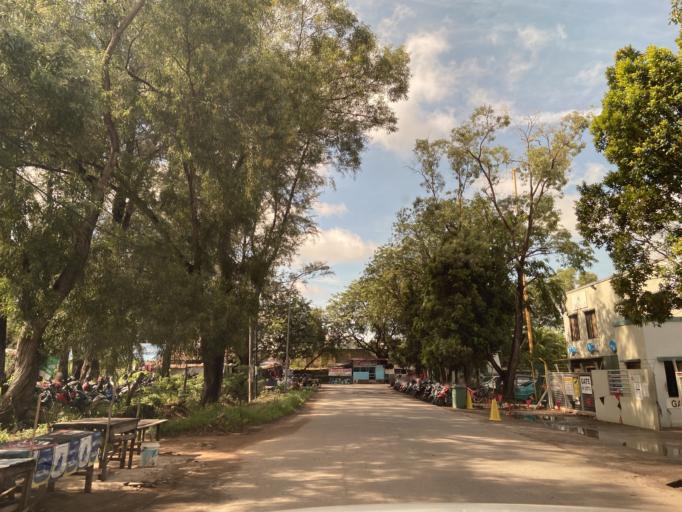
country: SG
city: Singapore
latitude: 1.1697
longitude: 104.0073
